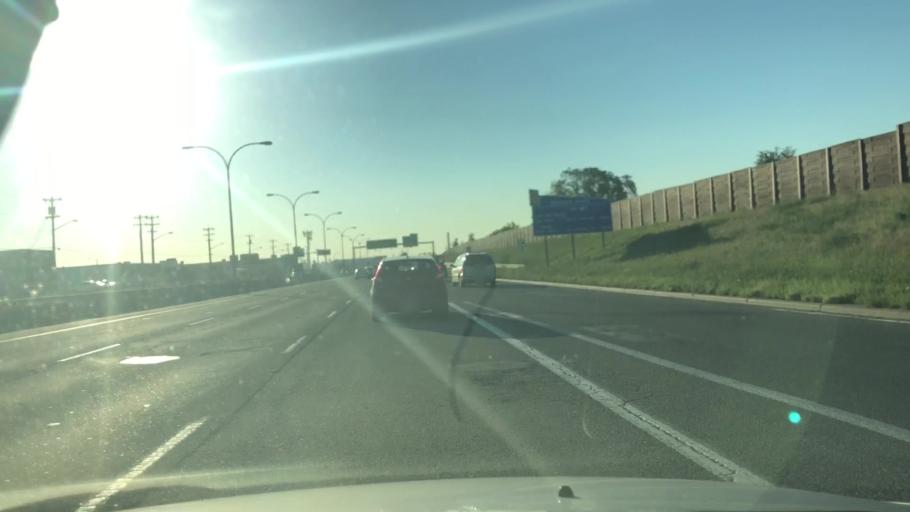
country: CA
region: Alberta
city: Edmonton
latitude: 53.5822
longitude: -113.4623
